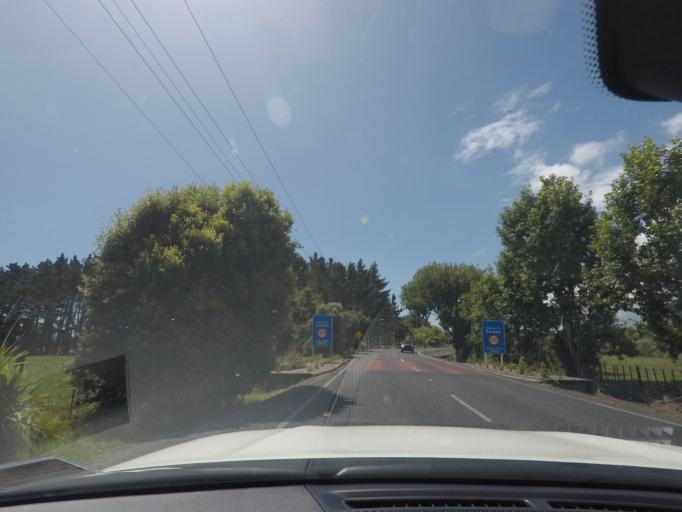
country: NZ
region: Auckland
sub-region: Auckland
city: Parakai
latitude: -36.6658
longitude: 174.4364
